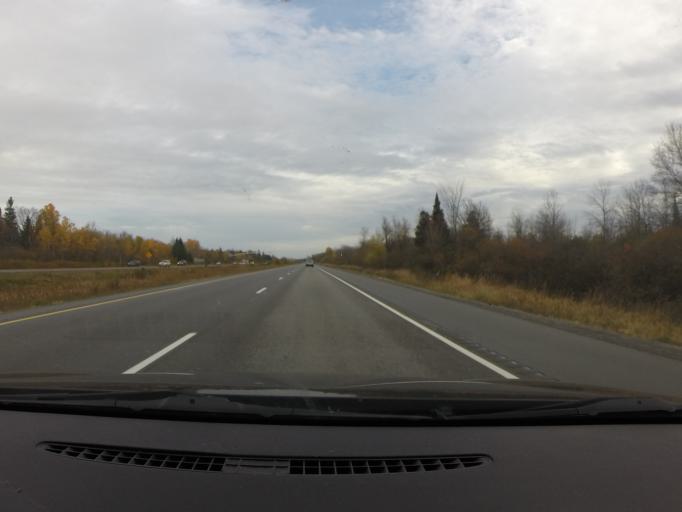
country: CA
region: Ontario
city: Bells Corners
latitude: 45.3059
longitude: -76.0358
